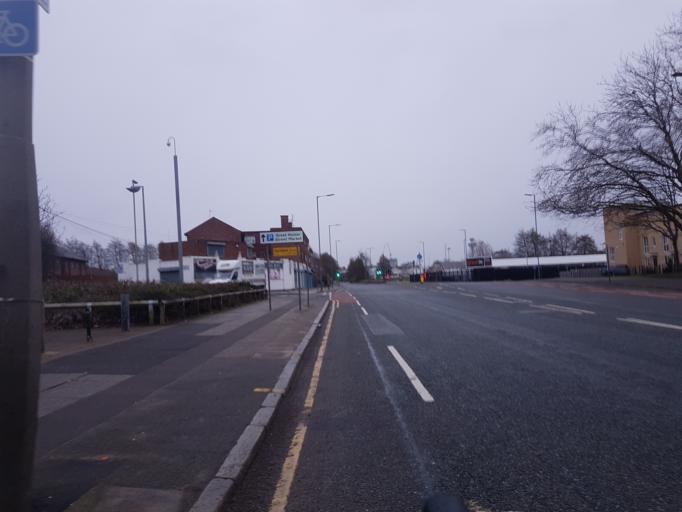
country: GB
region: England
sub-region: Liverpool
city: Liverpool
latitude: 53.4211
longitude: -2.9782
